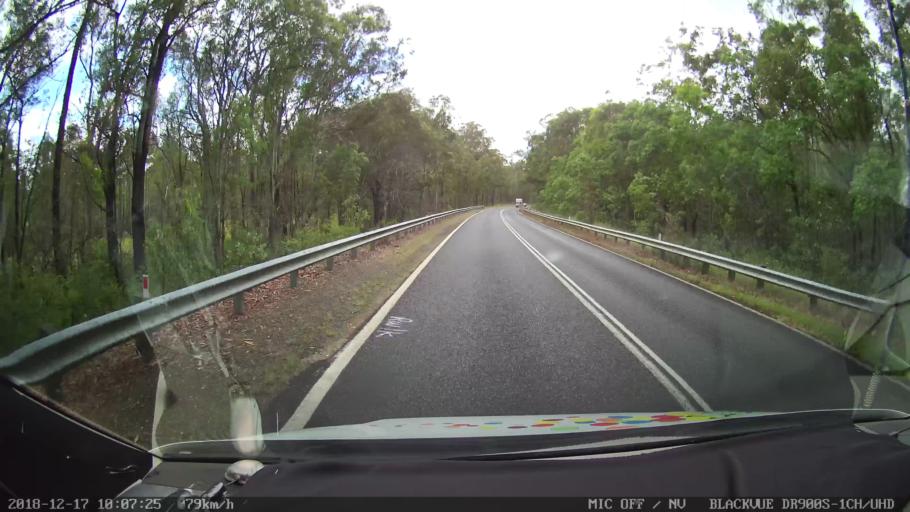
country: AU
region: New South Wales
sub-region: Tenterfield Municipality
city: Carrolls Creek
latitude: -28.8885
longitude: 152.5179
